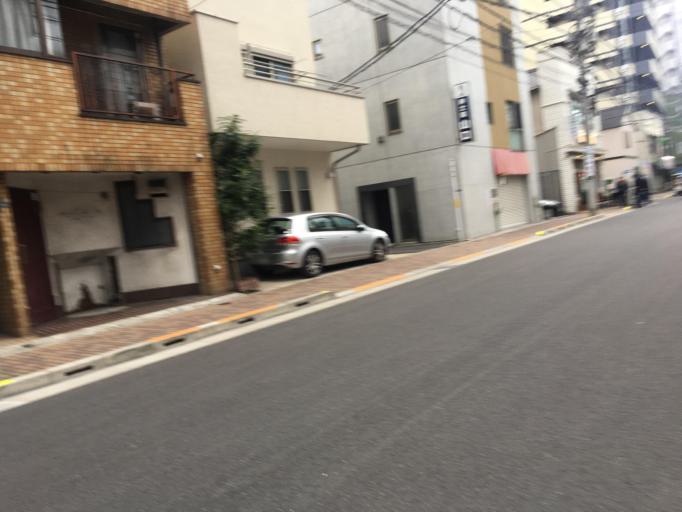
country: JP
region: Saitama
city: Soka
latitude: 35.7184
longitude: 139.7911
